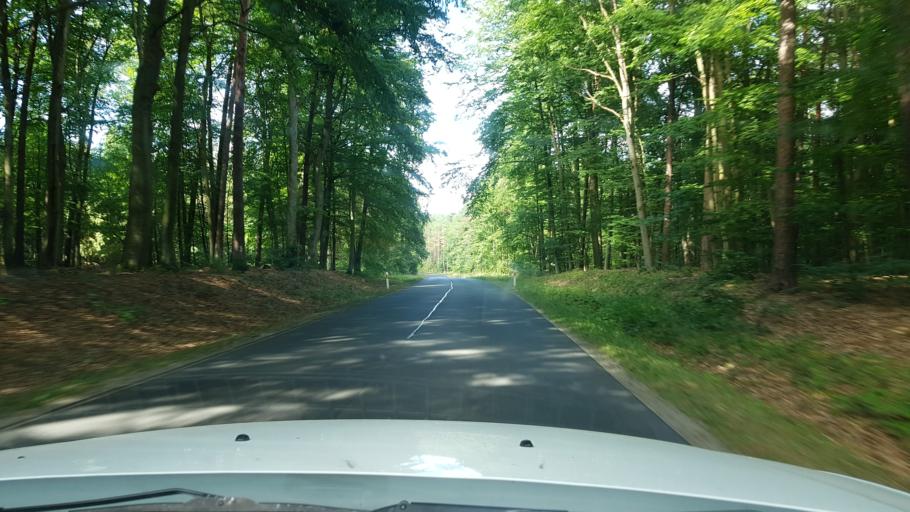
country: PL
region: West Pomeranian Voivodeship
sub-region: Powiat drawski
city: Zlocieniec
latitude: 53.5568
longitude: 16.0093
